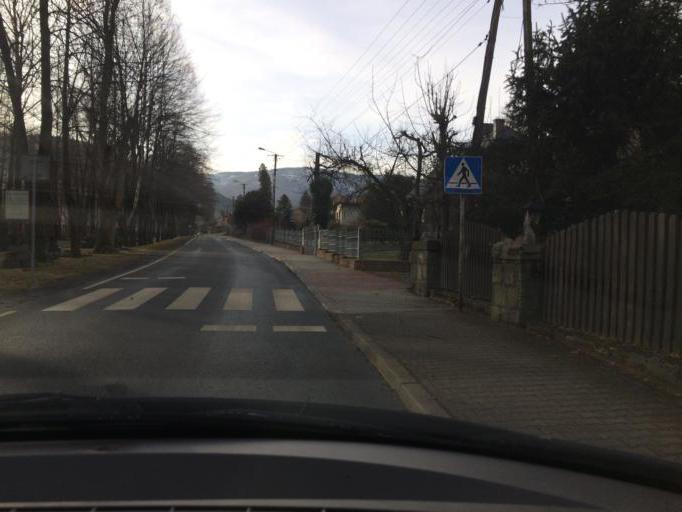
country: PL
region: Silesian Voivodeship
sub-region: Powiat bielski
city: Bystra
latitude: 49.7619
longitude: 19.0602
